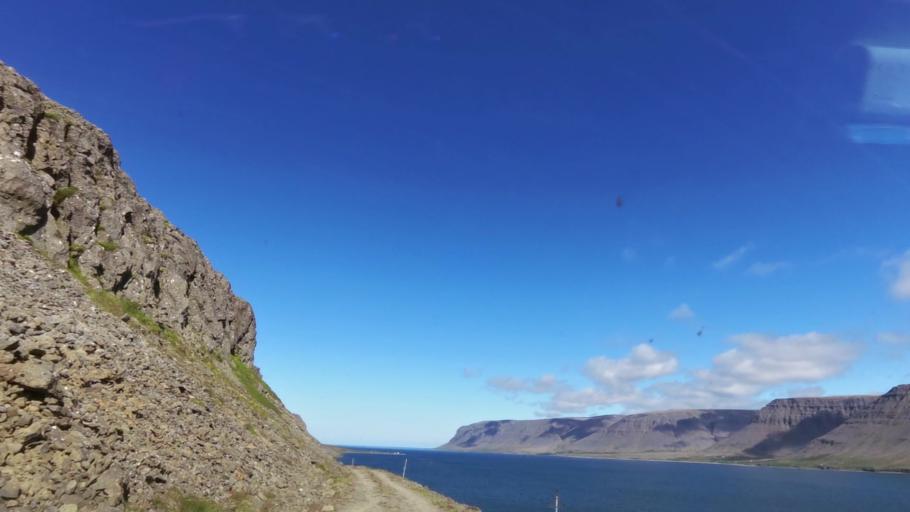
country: IS
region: West
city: Olafsvik
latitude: 65.6235
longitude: -23.8857
